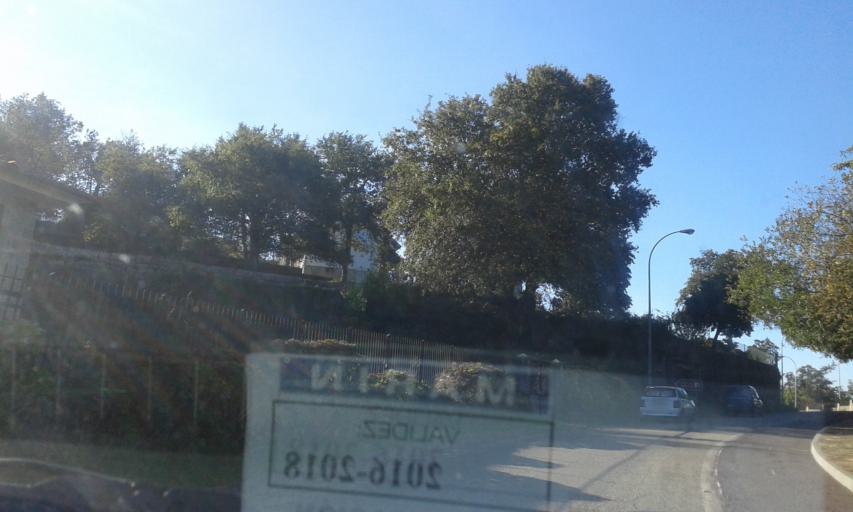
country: ES
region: Galicia
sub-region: Provincia de Pontevedra
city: Marin
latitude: 42.3809
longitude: -8.7252
